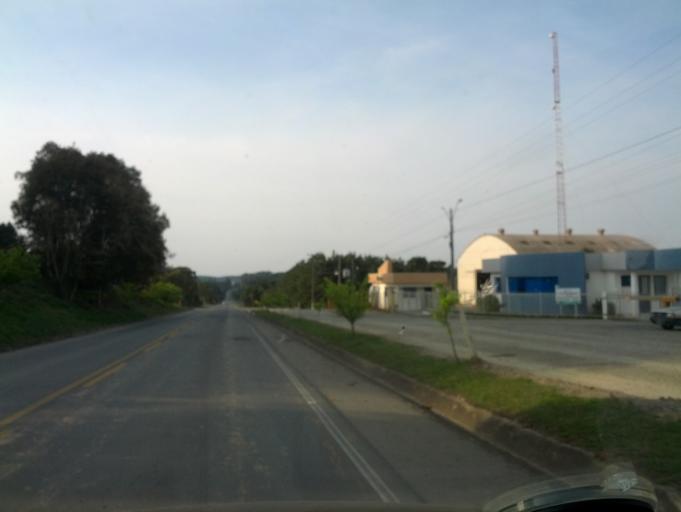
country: BR
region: Santa Catarina
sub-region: Otacilio Costa
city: Otacilio Costa
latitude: -27.5986
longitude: -50.1713
